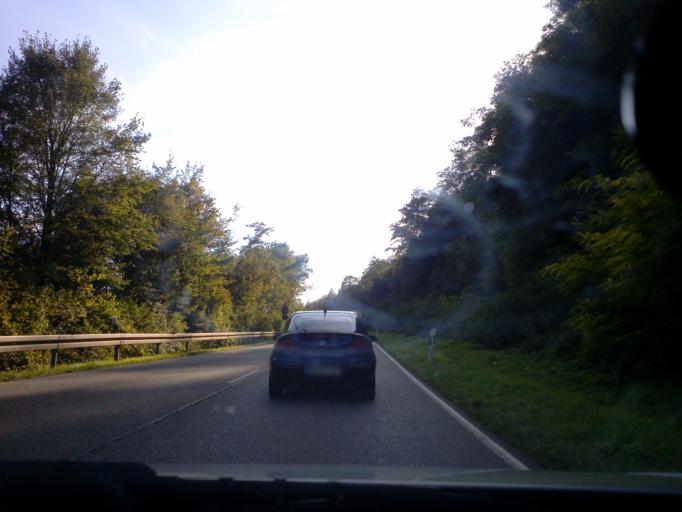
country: DE
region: Baden-Wuerttemberg
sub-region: Regierungsbezirk Stuttgart
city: Schwaigern
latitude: 49.1151
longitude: 9.0177
